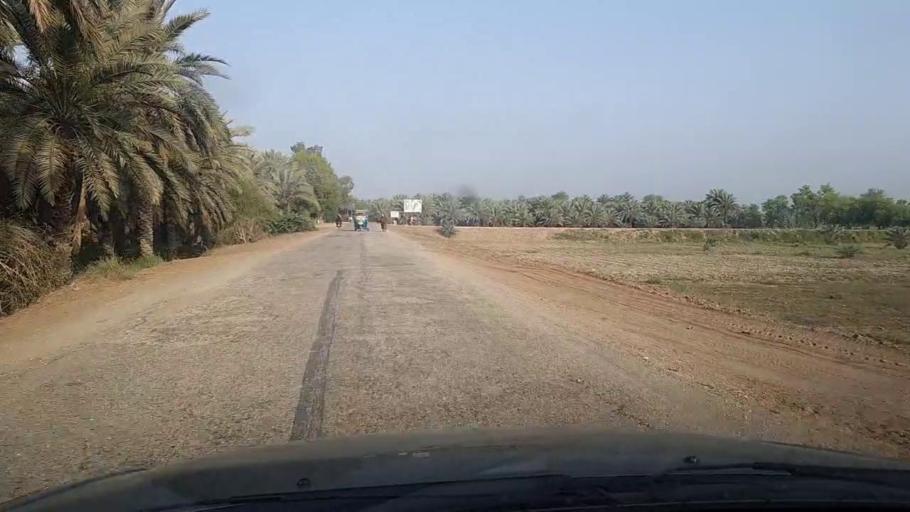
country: PK
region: Sindh
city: Pir jo Goth
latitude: 27.5550
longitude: 68.6807
